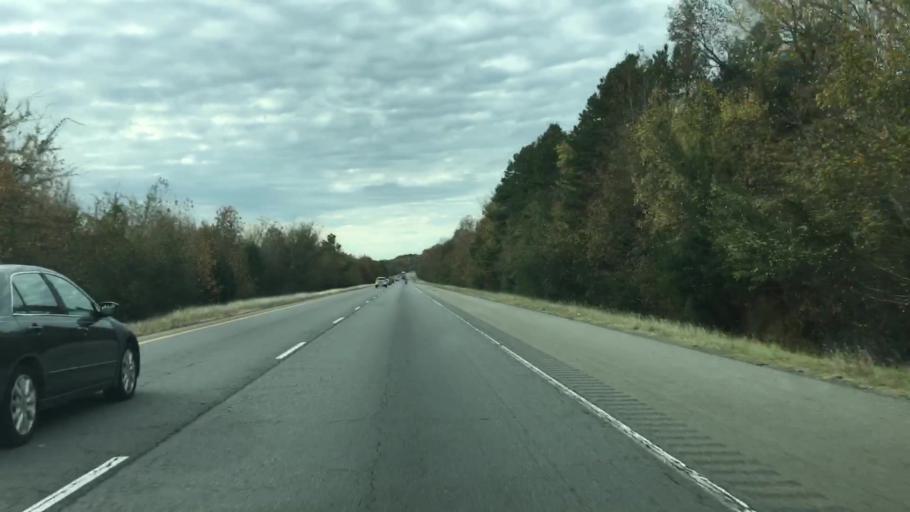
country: US
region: Arkansas
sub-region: Faulkner County
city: Conway
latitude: 35.1203
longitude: -92.4771
